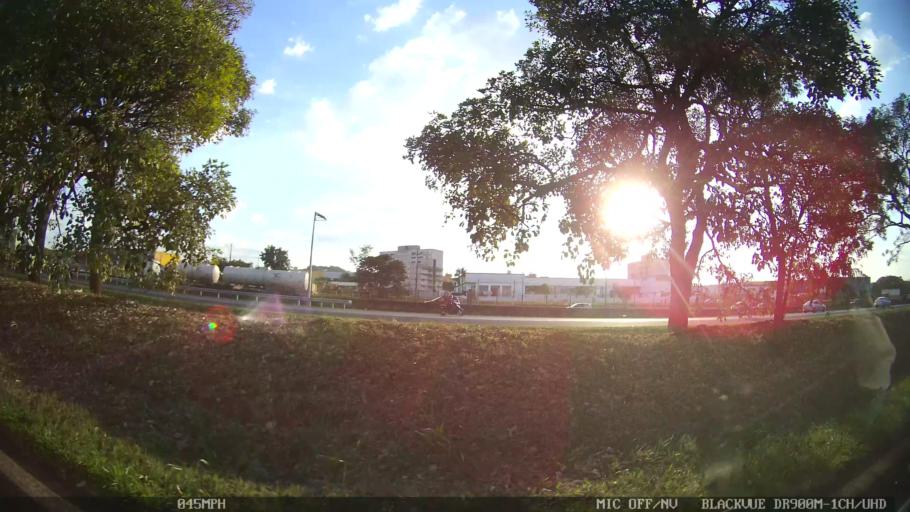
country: BR
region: Sao Paulo
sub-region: Ribeirao Preto
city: Ribeirao Preto
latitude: -21.1763
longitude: -47.7564
